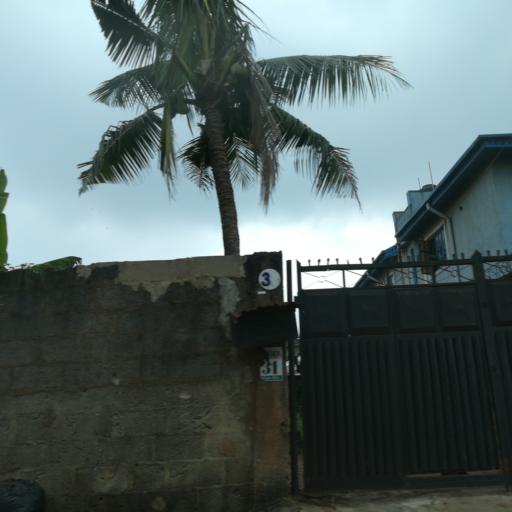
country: NG
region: Lagos
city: Oshodi
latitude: 6.5806
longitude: 3.3057
